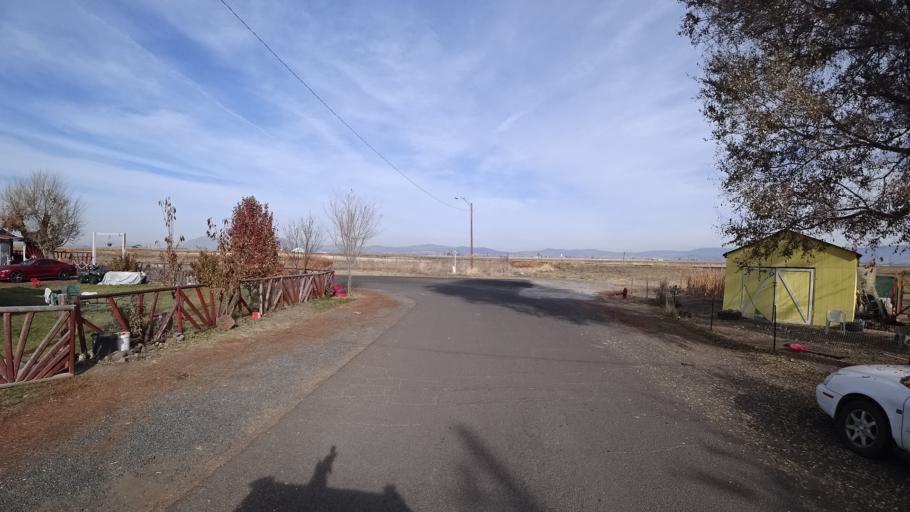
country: US
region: California
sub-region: Siskiyou County
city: Tulelake
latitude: 41.9604
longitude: -121.4792
